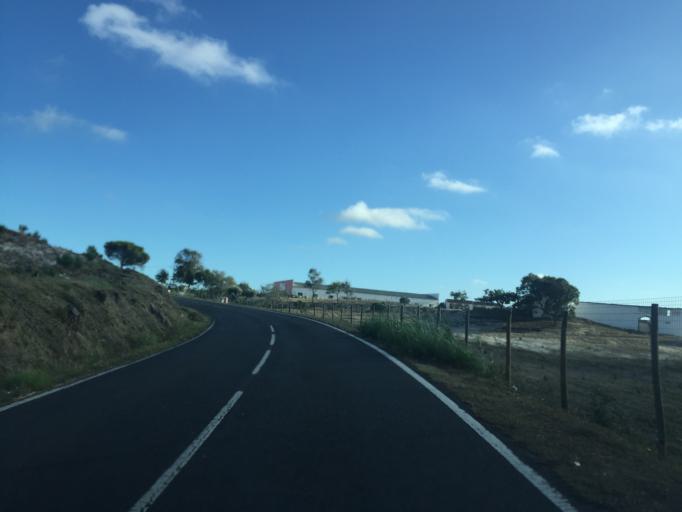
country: PT
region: Lisbon
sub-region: Torres Vedras
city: Torres Vedras
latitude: 39.1275
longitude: -9.2621
